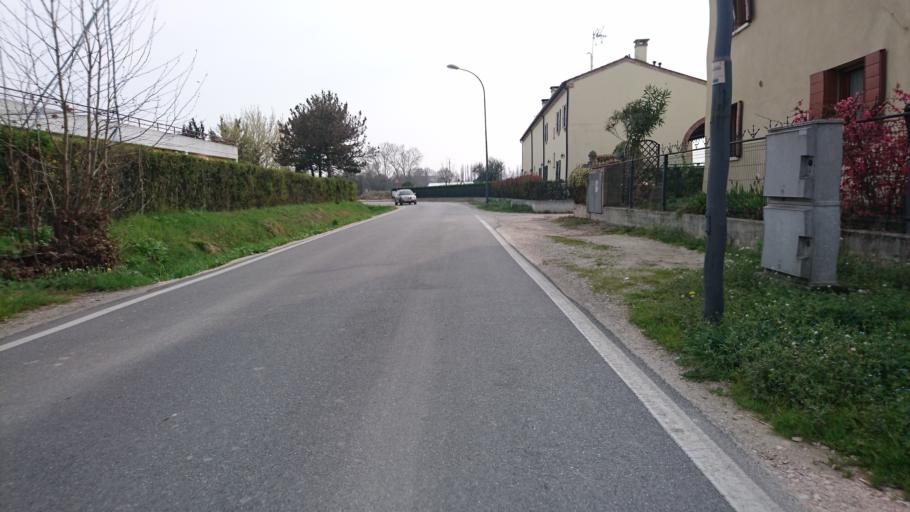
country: IT
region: Veneto
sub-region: Provincia di Padova
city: Abano Terme
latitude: 45.3664
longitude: 11.7844
